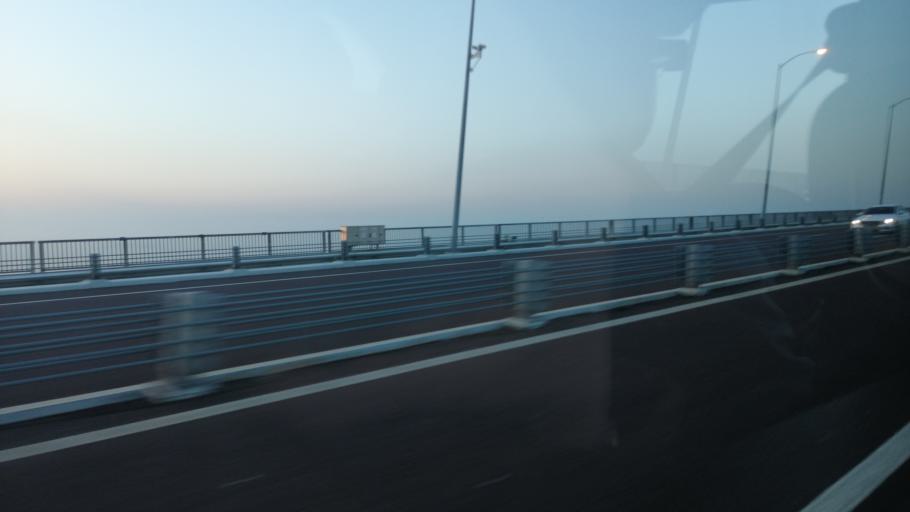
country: TR
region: Yalova
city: Altinova
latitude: 40.7373
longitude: 29.5125
